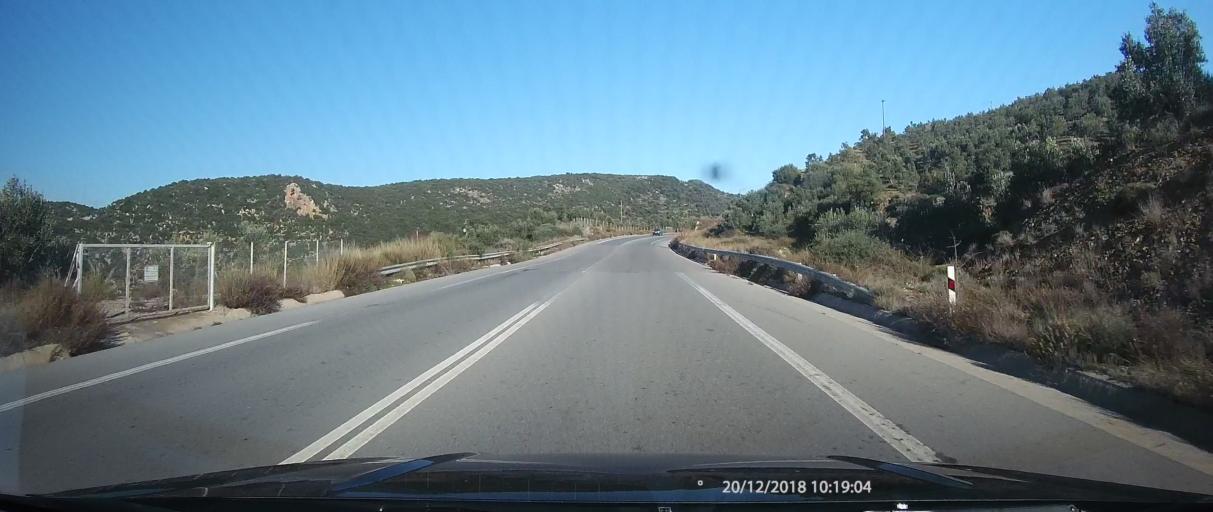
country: GR
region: Peloponnese
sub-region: Nomos Lakonias
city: Magoula
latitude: 37.1283
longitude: 22.4196
